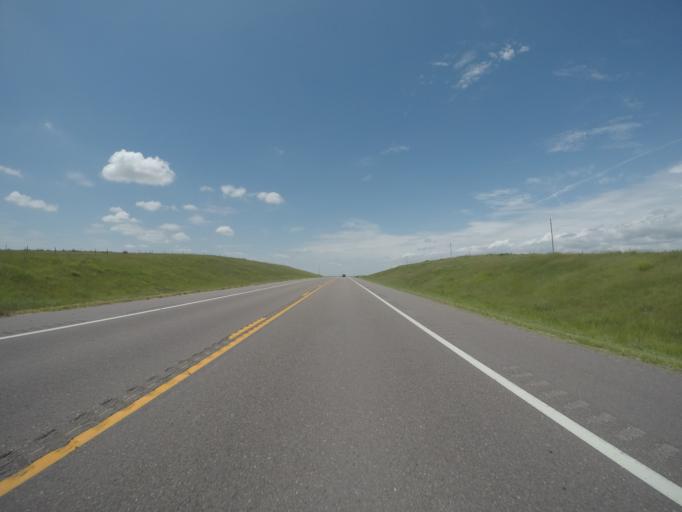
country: US
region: Kansas
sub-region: Graham County
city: Hill City
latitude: 39.3790
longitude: -99.7486
